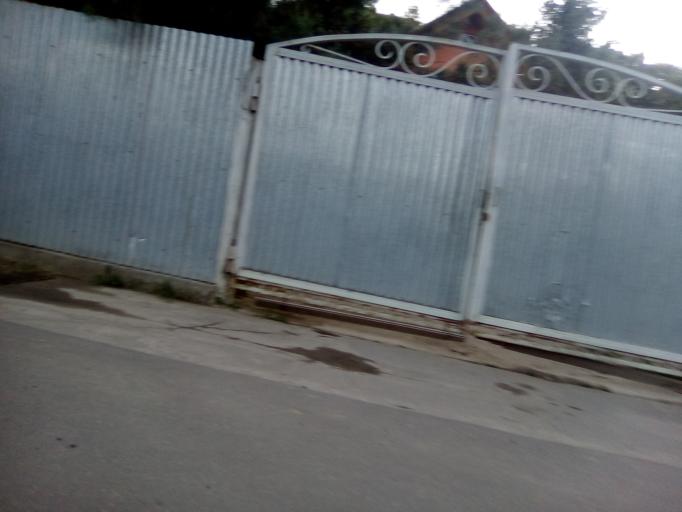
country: RU
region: Moskovskaya
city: Krasnoznamensk
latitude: 55.5762
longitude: 37.0364
